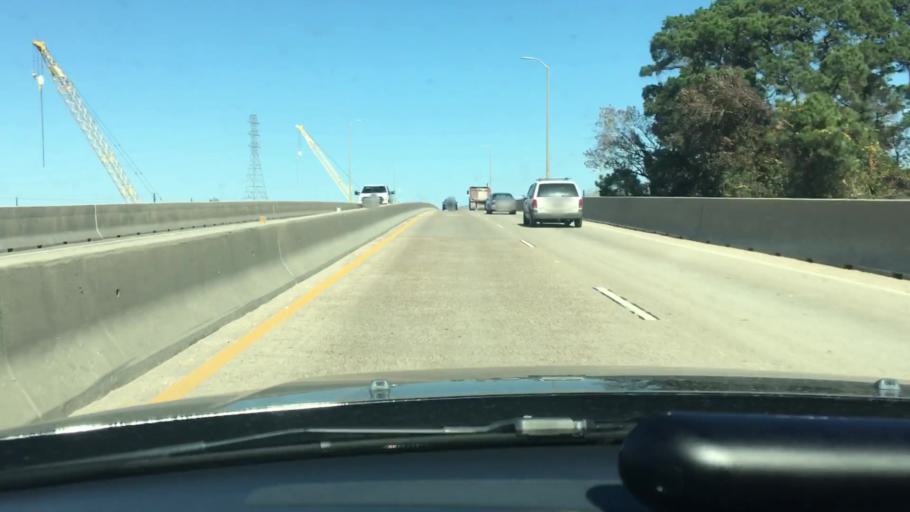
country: US
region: Texas
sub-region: Harris County
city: Cloverleaf
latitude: 29.7533
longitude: -95.1459
